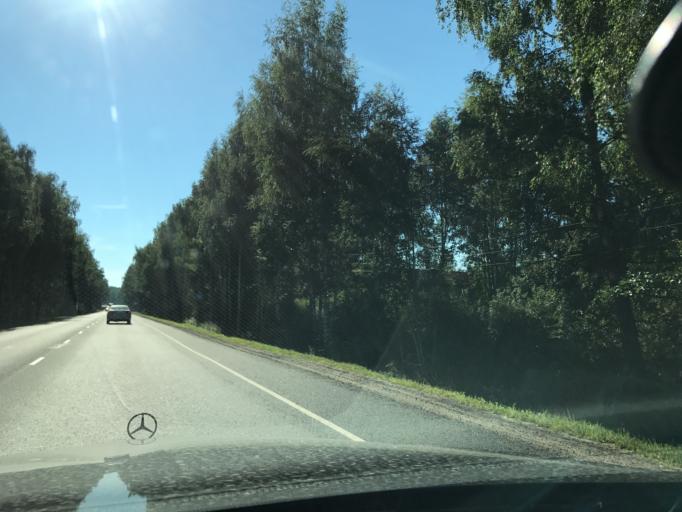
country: RU
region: Moskovskaya
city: Noginsk-9
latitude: 56.1019
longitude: 38.6532
